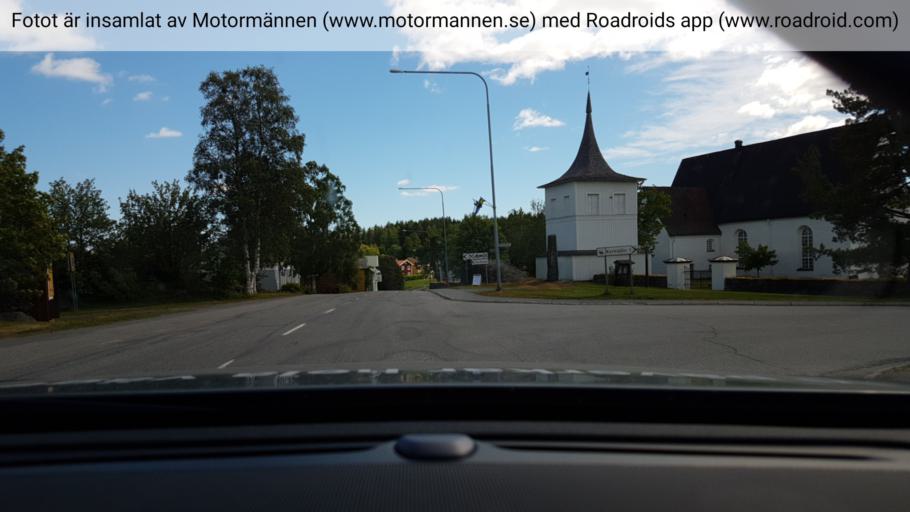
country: SE
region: Vaesterbotten
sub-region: Skelleftea Kommun
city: Burea
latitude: 64.3690
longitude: 21.3165
